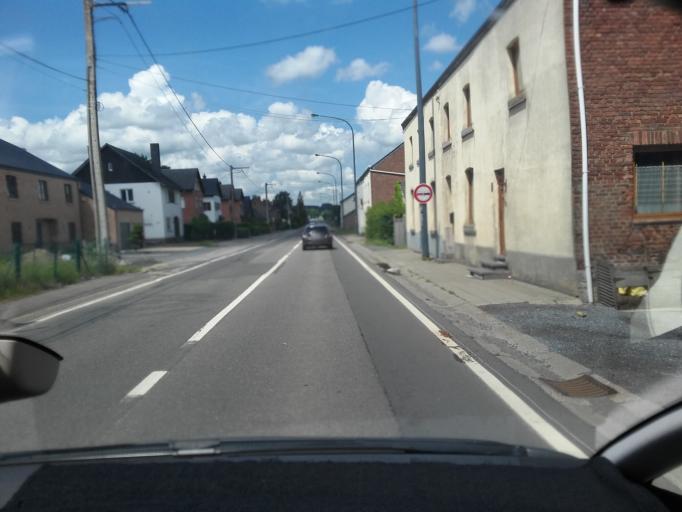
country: BE
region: Wallonia
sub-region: Province de Namur
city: Rochefort
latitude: 50.1700
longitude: 5.2115
